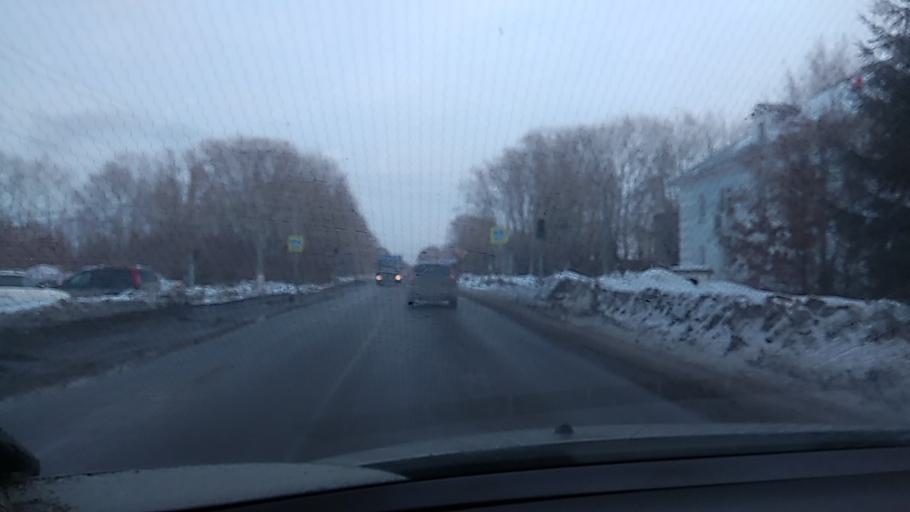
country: RU
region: Sverdlovsk
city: Martyush
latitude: 56.4458
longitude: 61.8181
